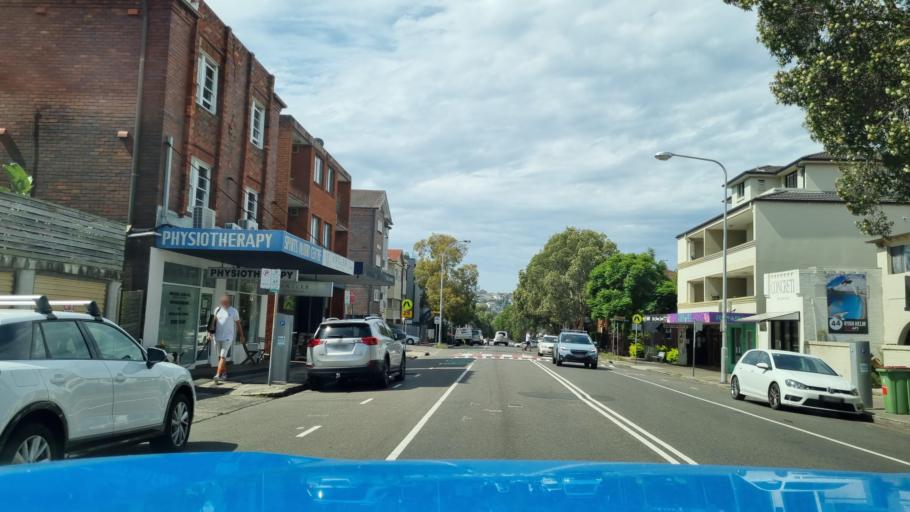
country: AU
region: New South Wales
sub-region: Waverley
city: Bondi Beach
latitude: -33.8886
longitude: 151.2708
